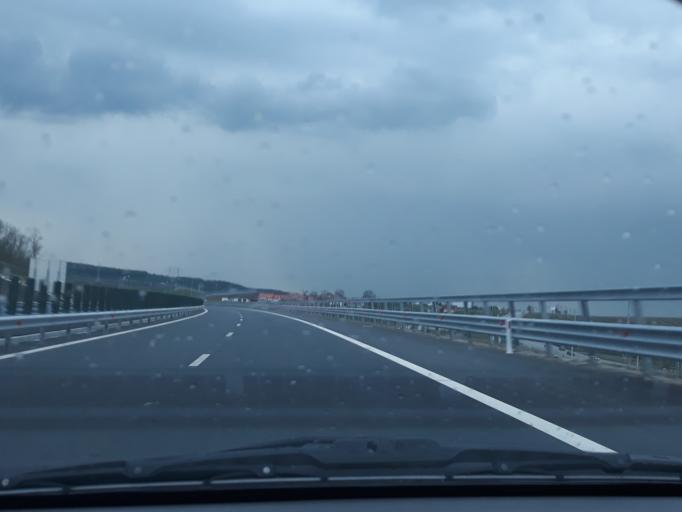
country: RO
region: Mures
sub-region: Comuna Sanpaul
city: Valea Izvoarelor
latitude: 46.4539
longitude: 24.3796
